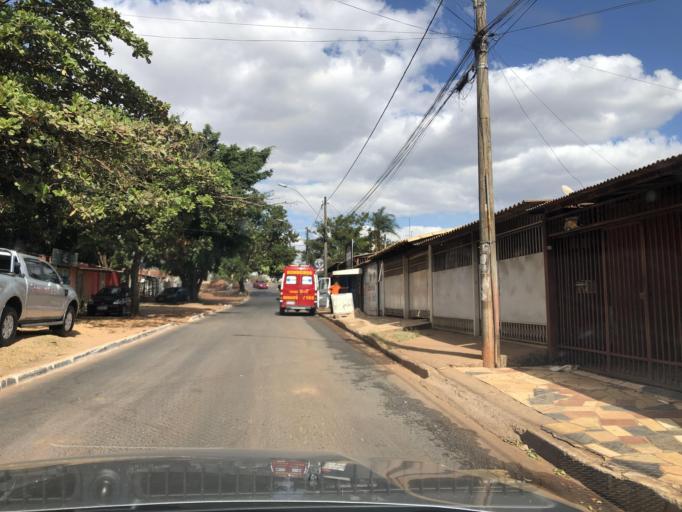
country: BR
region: Federal District
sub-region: Brasilia
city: Brasilia
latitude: -15.8884
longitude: -48.1427
